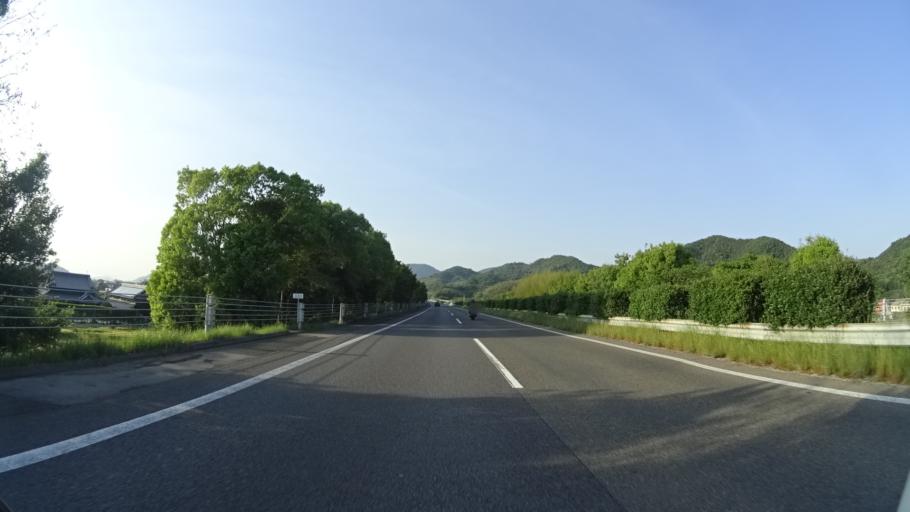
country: JP
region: Kagawa
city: Kan'onjicho
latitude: 34.1715
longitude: 133.7332
